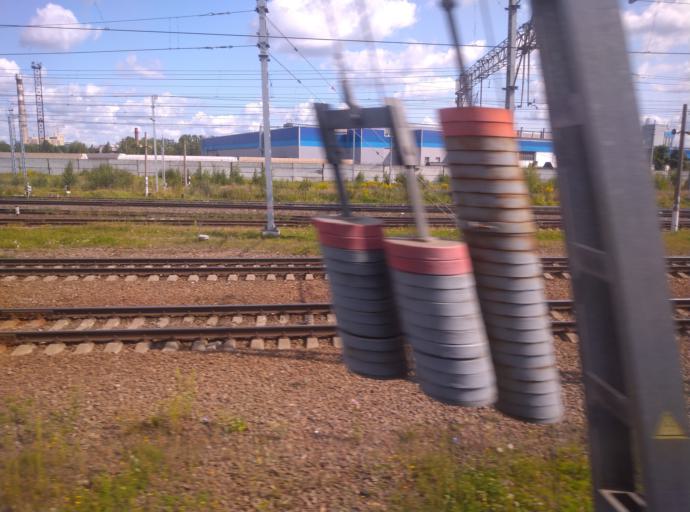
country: RU
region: St.-Petersburg
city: Obukhovo
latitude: 59.8501
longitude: 30.4524
